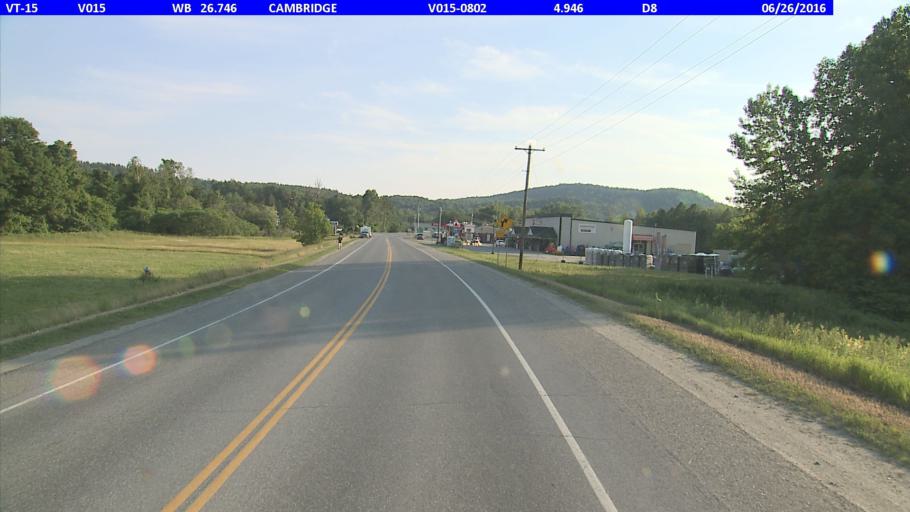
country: US
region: Vermont
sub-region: Lamoille County
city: Johnson
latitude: 44.6463
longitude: -72.8325
